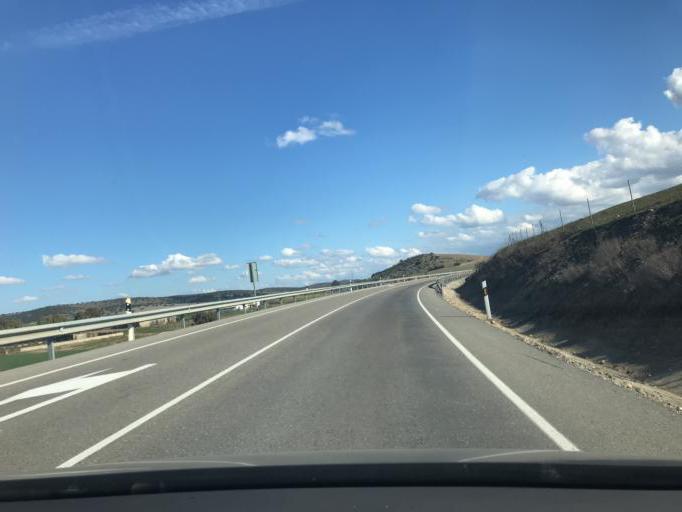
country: ES
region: Andalusia
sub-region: Province of Cordoba
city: Penarroya-Pueblonuevo
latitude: 38.3102
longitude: -5.2688
